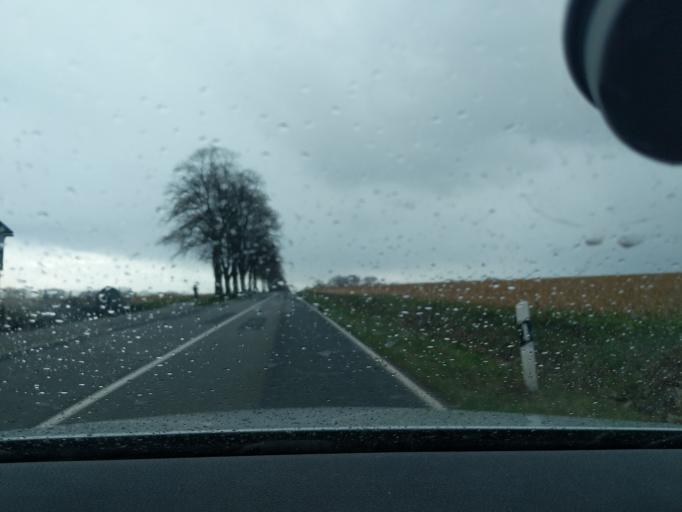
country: DE
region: Lower Saxony
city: Bargstedt
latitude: 53.4615
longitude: 9.4616
